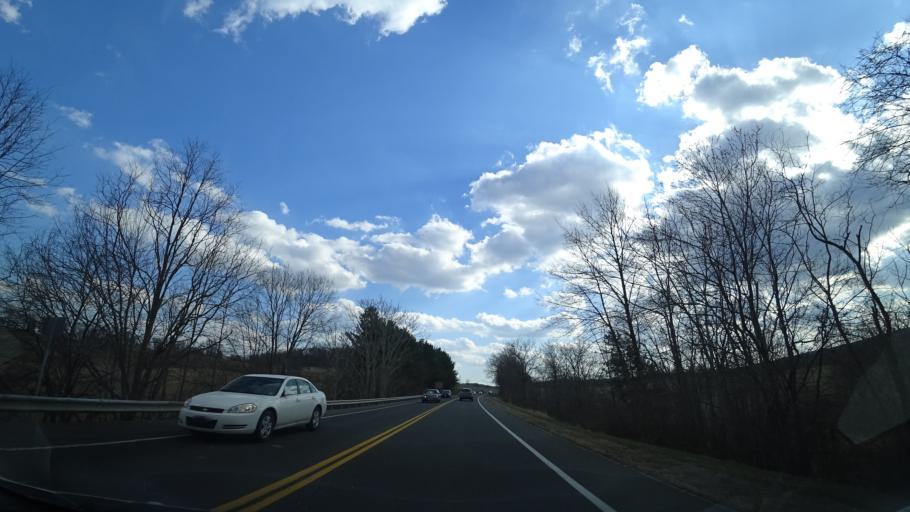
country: US
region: Virginia
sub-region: Warren County
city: Shenandoah Farms
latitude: 38.9841
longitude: -77.9491
